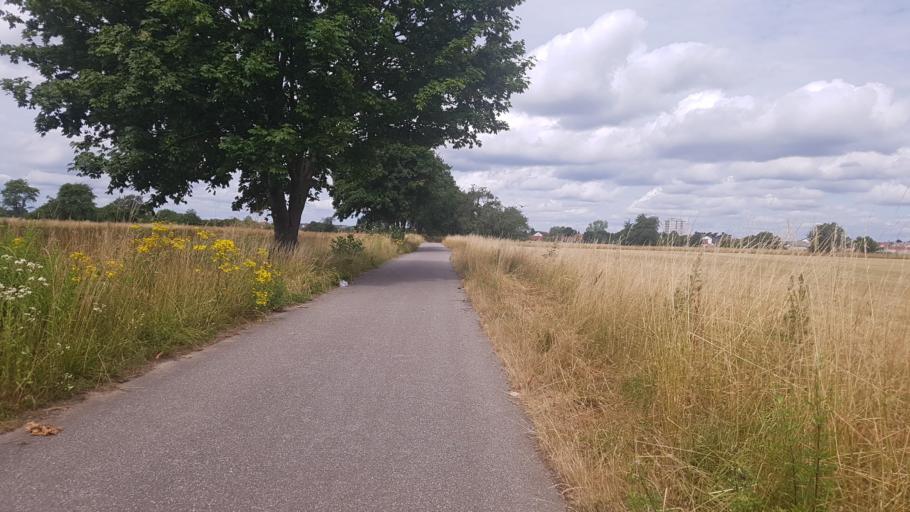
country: DE
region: Baden-Wuerttemberg
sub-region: Karlsruhe Region
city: Rheinstetten
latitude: 48.9735
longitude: 8.3282
